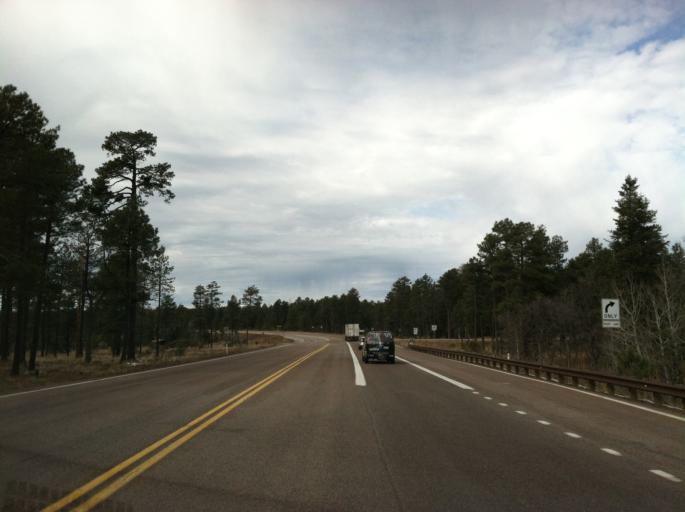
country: US
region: Arizona
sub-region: Navajo County
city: Heber-Overgaard
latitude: 34.3022
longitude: -110.8895
